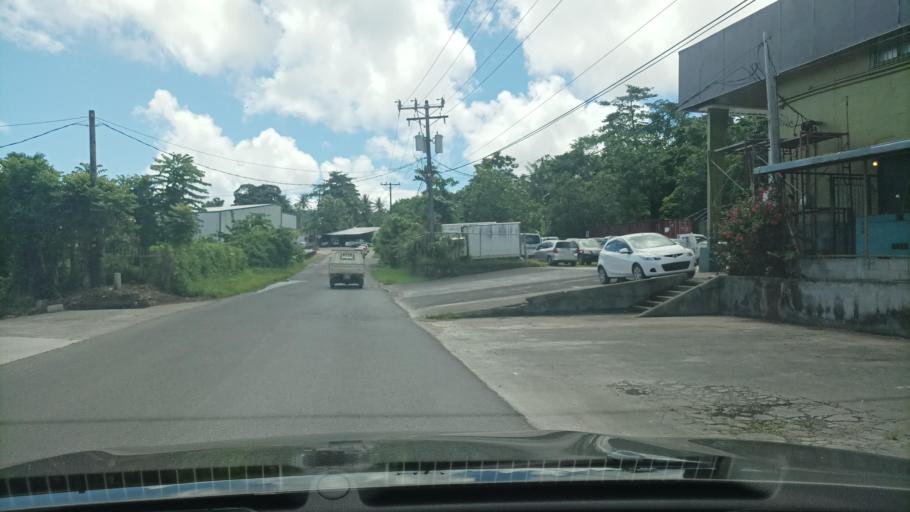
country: FM
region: Pohnpei
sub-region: Kolonia Municipality
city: Kolonia Town
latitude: 6.9570
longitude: 158.2046
